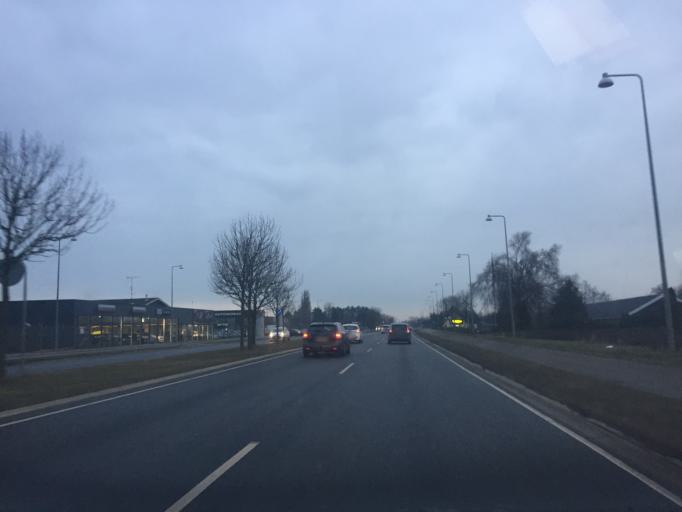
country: DK
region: Zealand
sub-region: Solrod Kommune
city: Solrod
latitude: 55.5030
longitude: 12.1985
